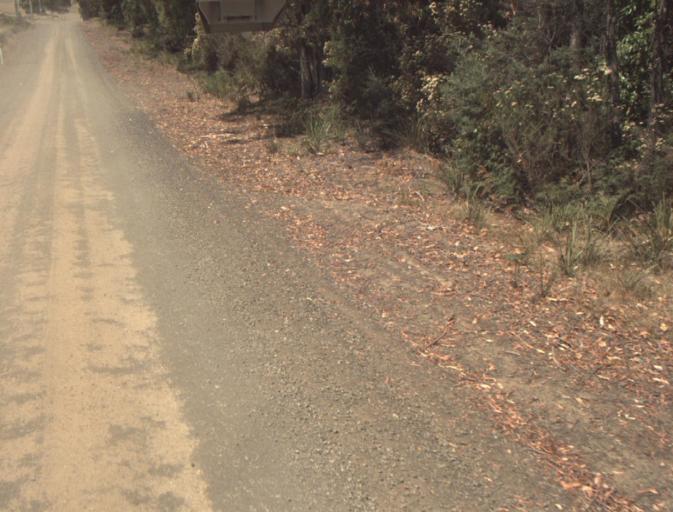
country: AU
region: Tasmania
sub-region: Launceston
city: Newstead
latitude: -41.3474
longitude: 147.3743
